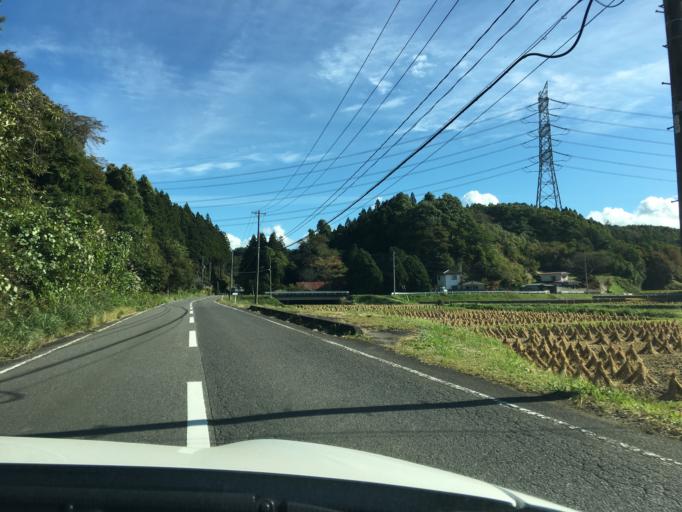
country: JP
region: Fukushima
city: Ishikawa
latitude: 37.1826
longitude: 140.5878
